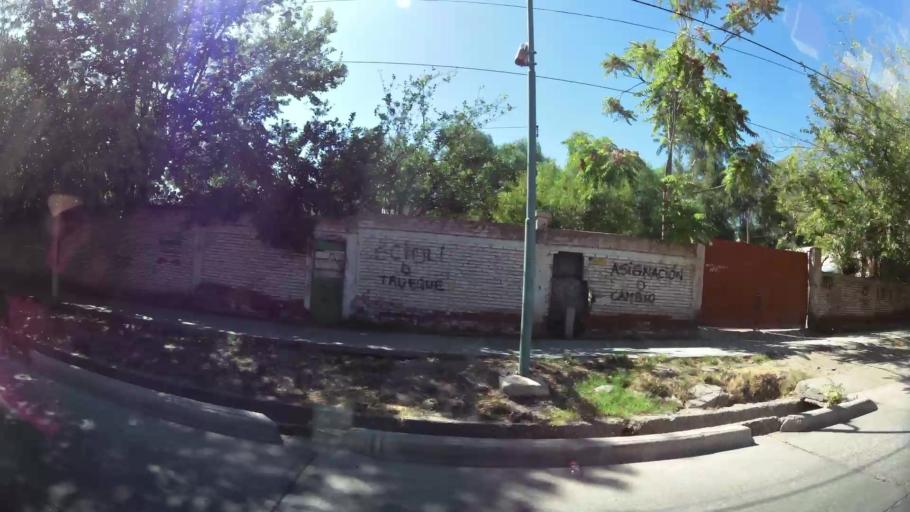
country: AR
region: Mendoza
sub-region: Departamento de Godoy Cruz
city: Godoy Cruz
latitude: -32.9086
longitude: -68.8708
